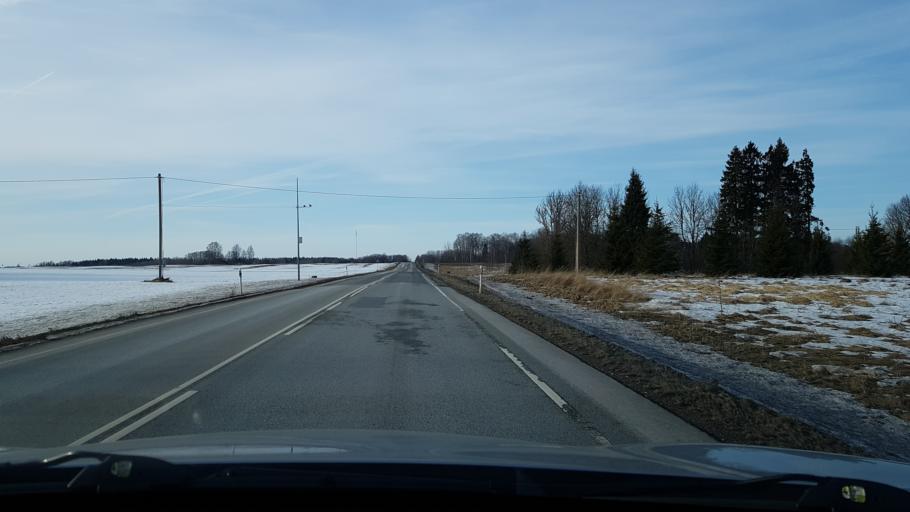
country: EE
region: Viljandimaa
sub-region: Viljandi linn
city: Viljandi
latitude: 58.3544
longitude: 25.4408
